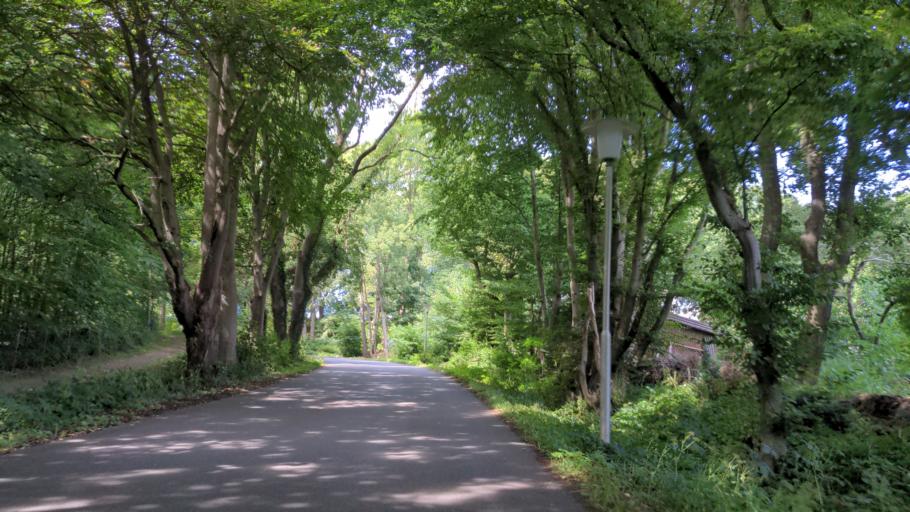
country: DE
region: Schleswig-Holstein
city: Eutin
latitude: 54.1881
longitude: 10.6108
